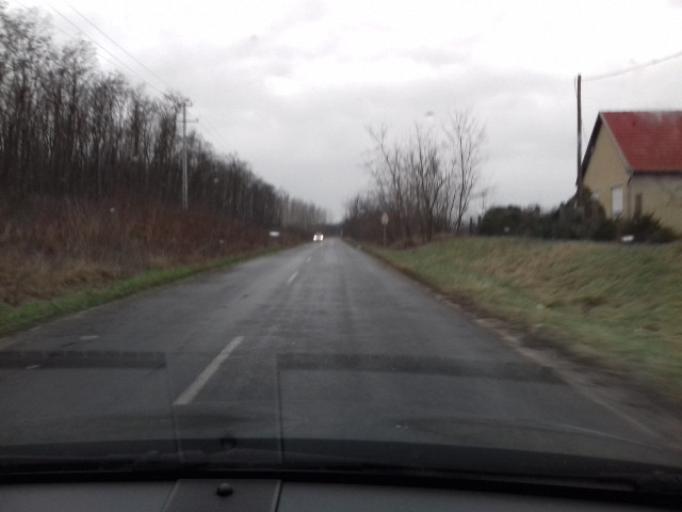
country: HU
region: Szabolcs-Szatmar-Bereg
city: Kek
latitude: 48.0951
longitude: 21.8808
